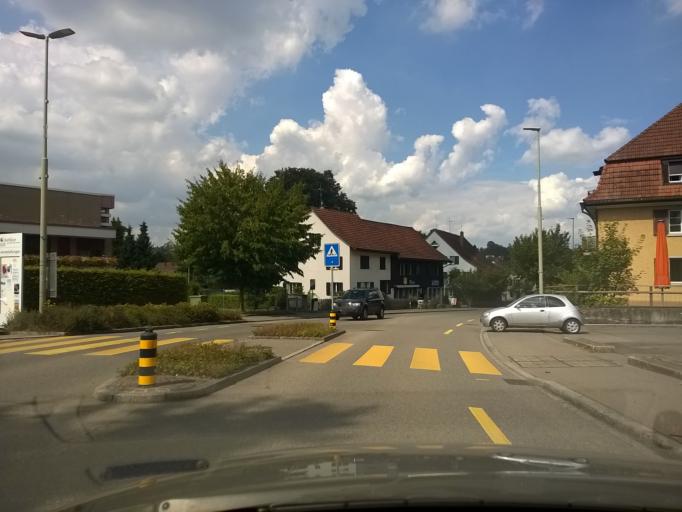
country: CH
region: Zurich
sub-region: Bezirk Buelach
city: Dietlikon / Eichwiesen
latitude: 47.4237
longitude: 8.6178
